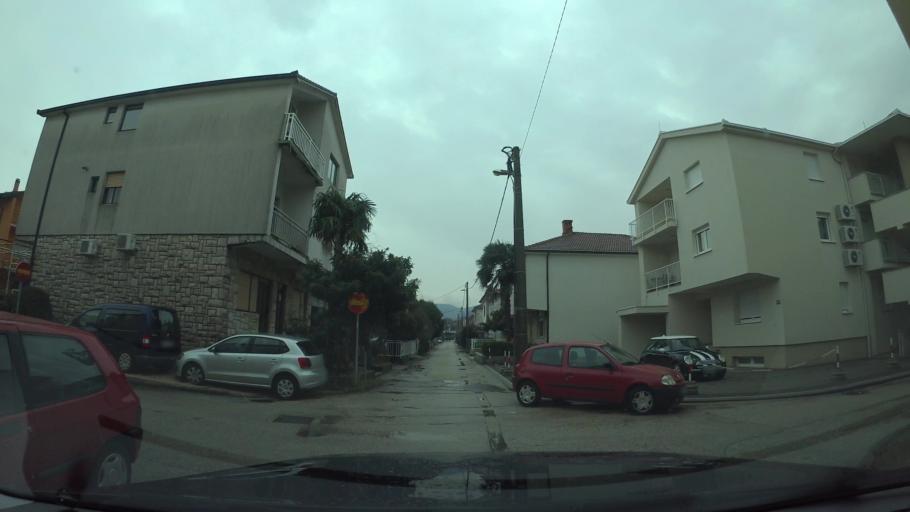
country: BA
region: Federation of Bosnia and Herzegovina
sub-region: Hercegovacko-Bosanski Kanton
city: Mostar
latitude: 43.3553
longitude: 17.8016
